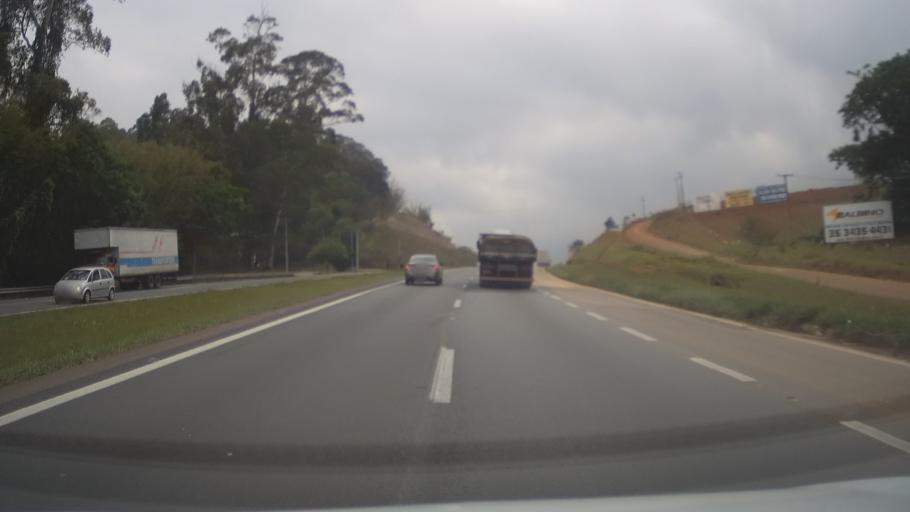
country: BR
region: Minas Gerais
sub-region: Extrema
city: Extrema
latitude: -22.8821
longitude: -46.3846
